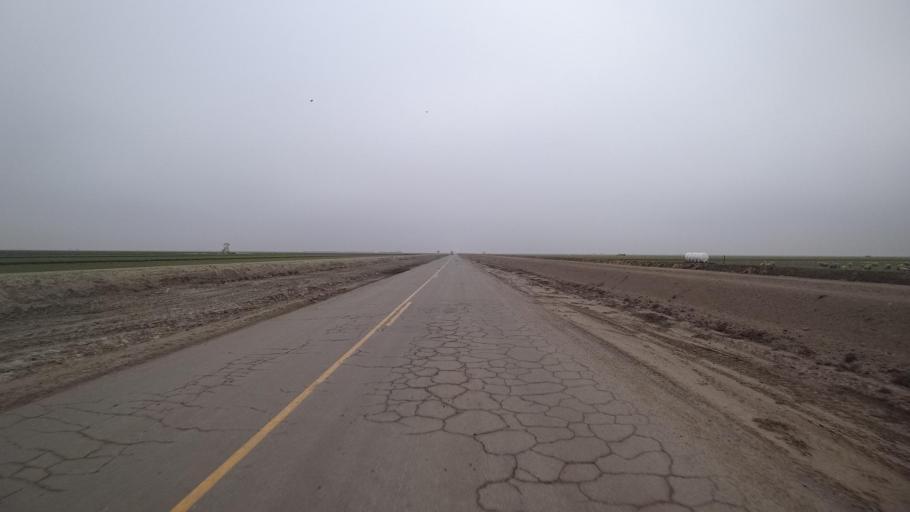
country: US
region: California
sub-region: Kern County
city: Rosedale
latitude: 35.1934
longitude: -119.1991
